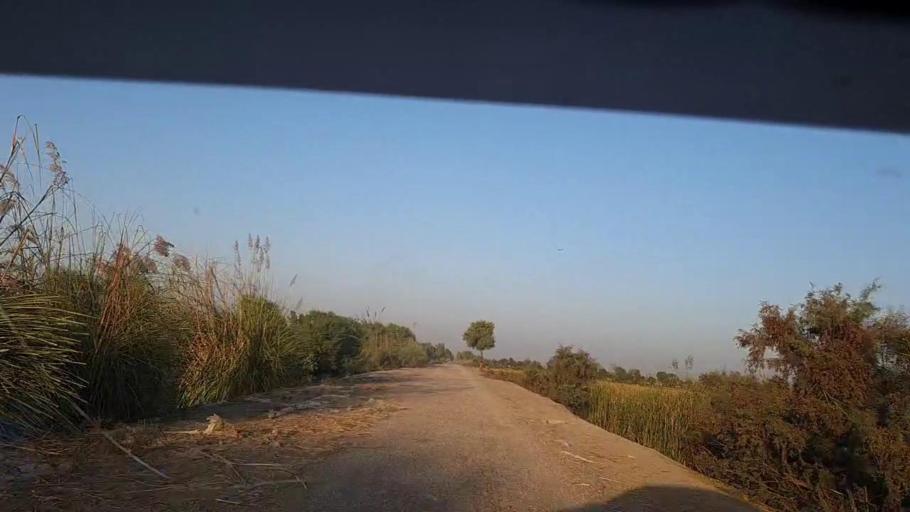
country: PK
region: Sindh
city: Ratodero
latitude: 27.8856
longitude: 68.2126
